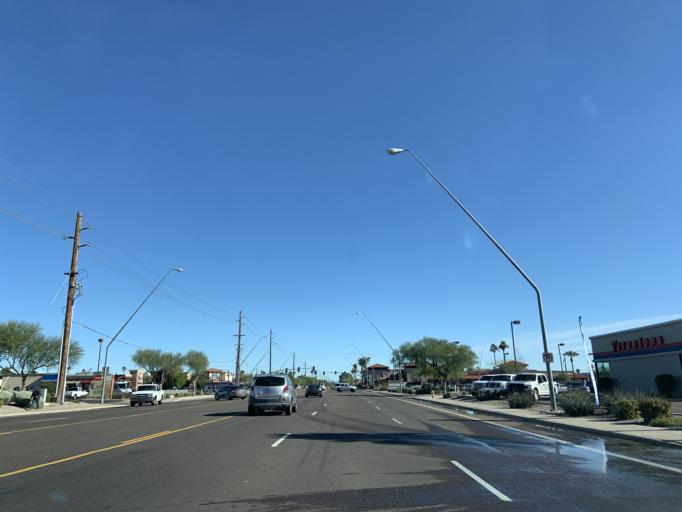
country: US
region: Arizona
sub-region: Maricopa County
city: San Carlos
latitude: 33.3642
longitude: -111.8611
